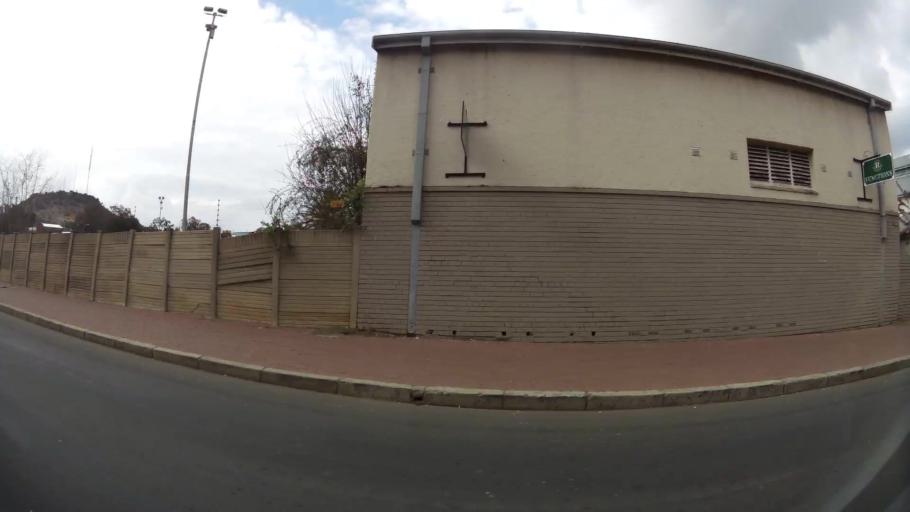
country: ZA
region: Orange Free State
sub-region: Mangaung Metropolitan Municipality
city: Bloemfontein
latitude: -29.1112
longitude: 26.2197
